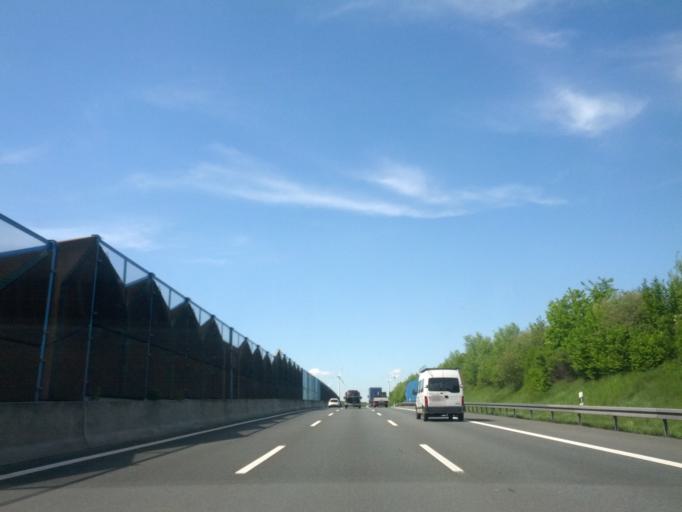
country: DE
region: Saxony
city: Neukirchen
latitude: 50.8230
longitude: 12.8539
